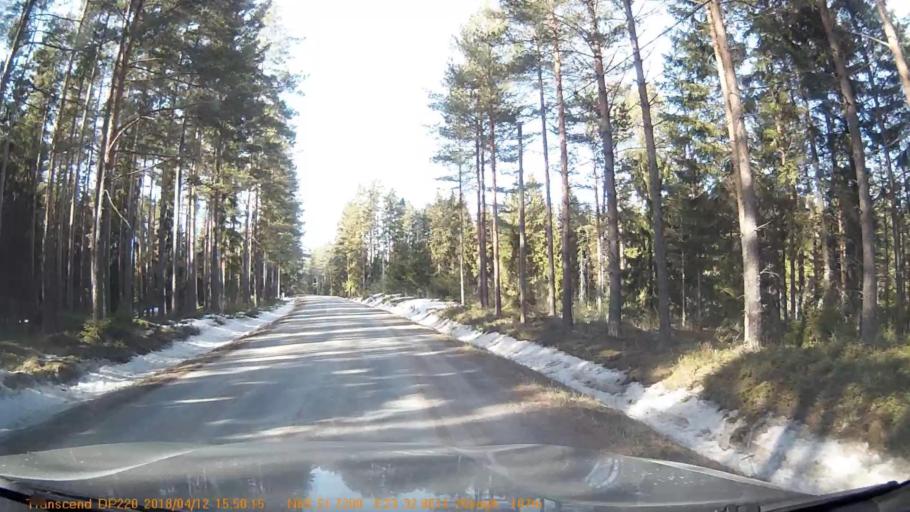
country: FI
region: Haeme
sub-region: Forssa
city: Forssa
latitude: 60.8621
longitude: 23.5477
